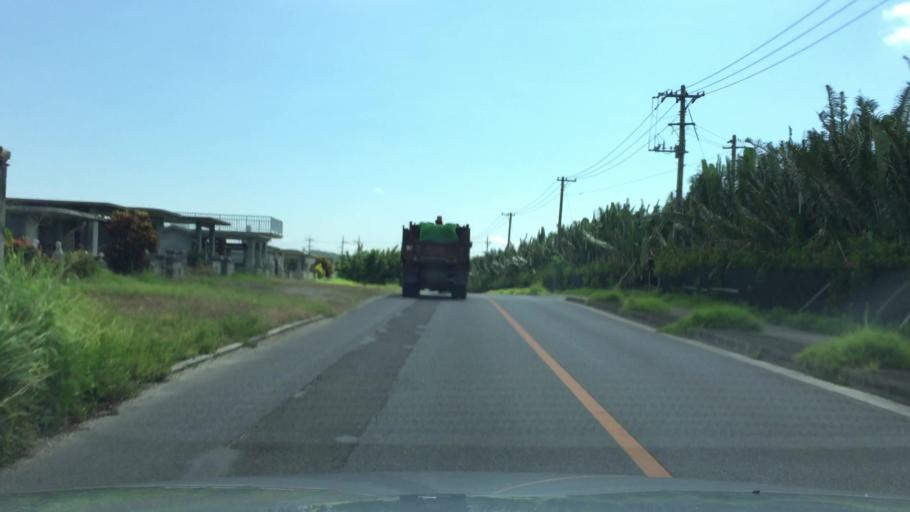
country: JP
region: Okinawa
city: Ishigaki
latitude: 24.3566
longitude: 124.1983
